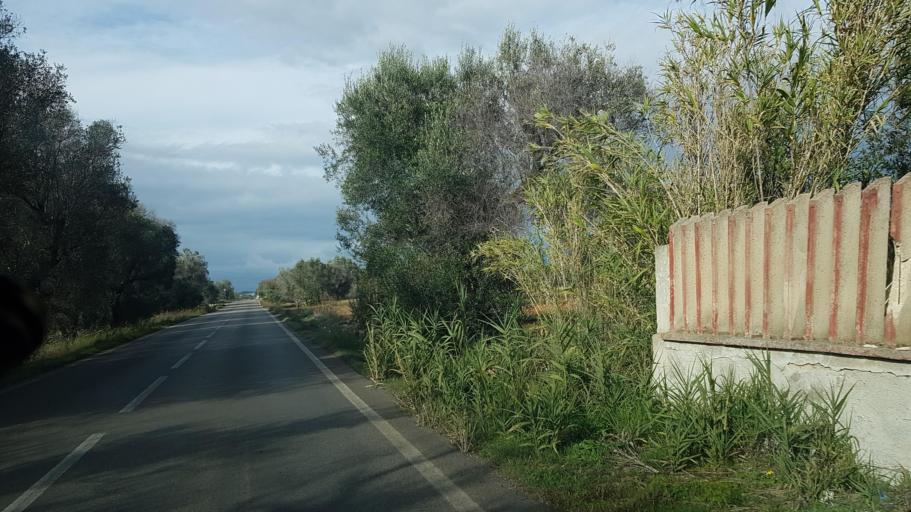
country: IT
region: Apulia
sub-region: Provincia di Brindisi
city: Torre Santa Susanna
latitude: 40.4764
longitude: 17.6998
